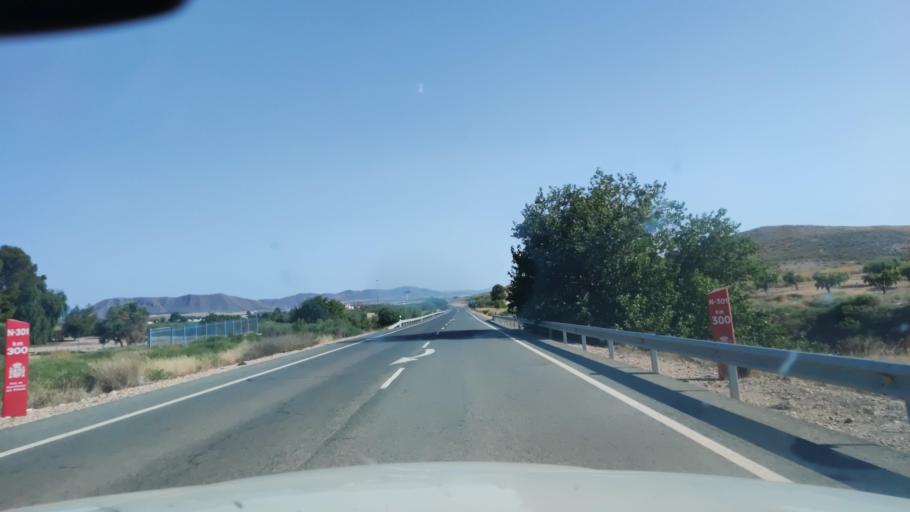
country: ES
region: Castille-La Mancha
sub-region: Provincia de Albacete
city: Tobarra
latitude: 38.6103
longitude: -1.6826
